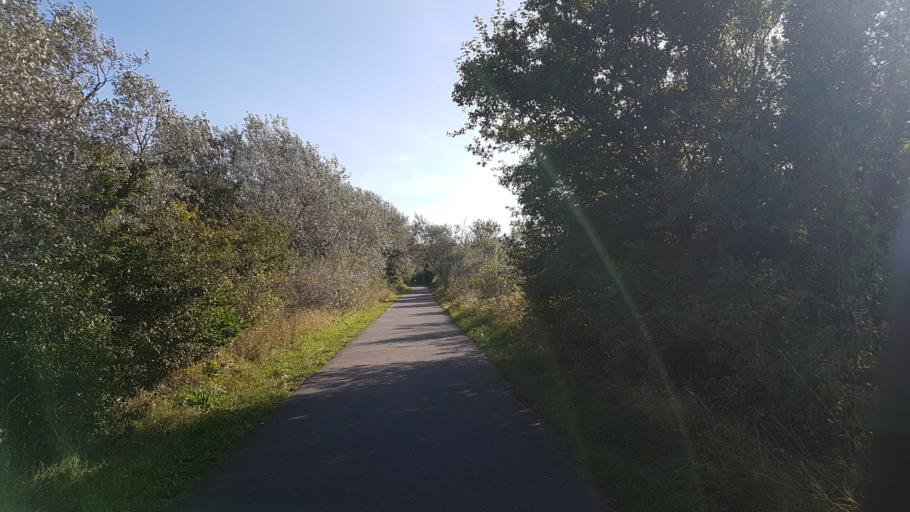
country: DE
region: Mecklenburg-Vorpommern
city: Wiek
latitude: 54.6372
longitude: 13.2909
